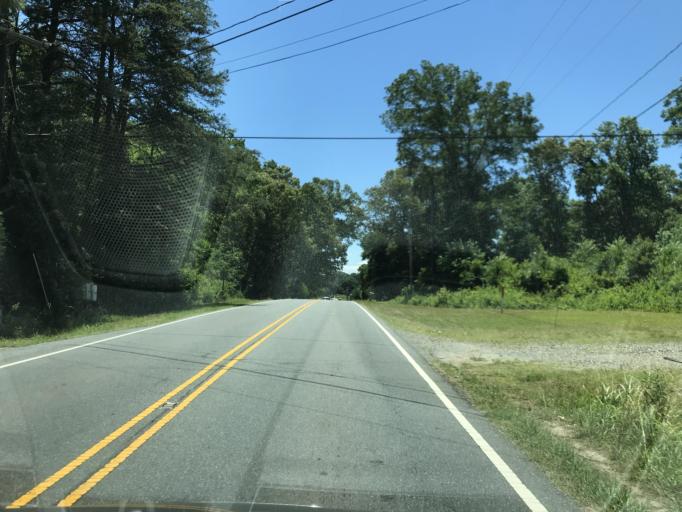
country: US
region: North Carolina
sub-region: Gaston County
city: Dallas
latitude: 35.3285
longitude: -81.1977
